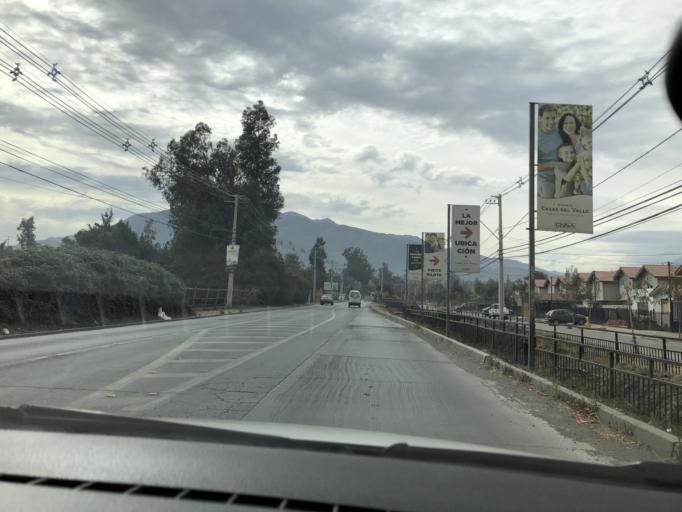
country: CL
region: Santiago Metropolitan
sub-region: Provincia de Cordillera
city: Puente Alto
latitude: -33.6096
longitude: -70.5401
